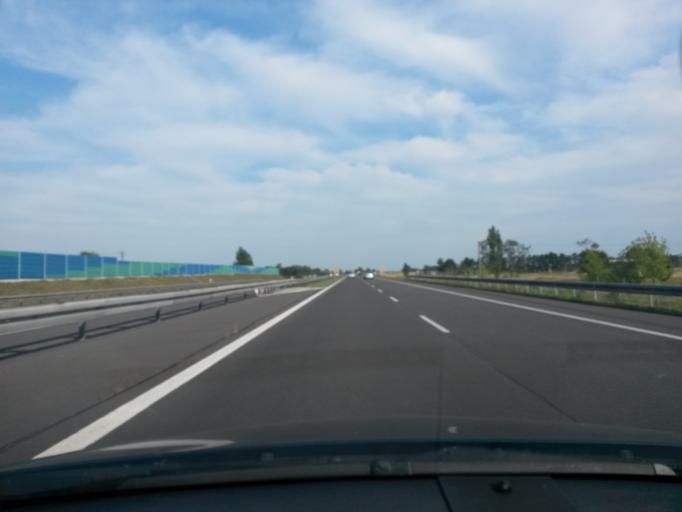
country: PL
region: Greater Poland Voivodeship
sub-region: Powiat slupecki
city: Slupca
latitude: 52.2434
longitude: 17.8677
